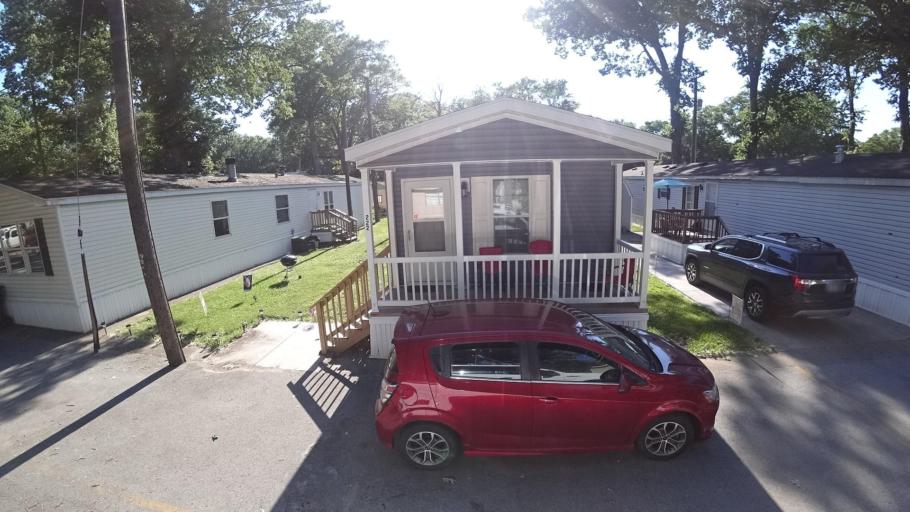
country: US
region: Indiana
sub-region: Porter County
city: Burns Harbor
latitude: 41.6159
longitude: -87.1418
